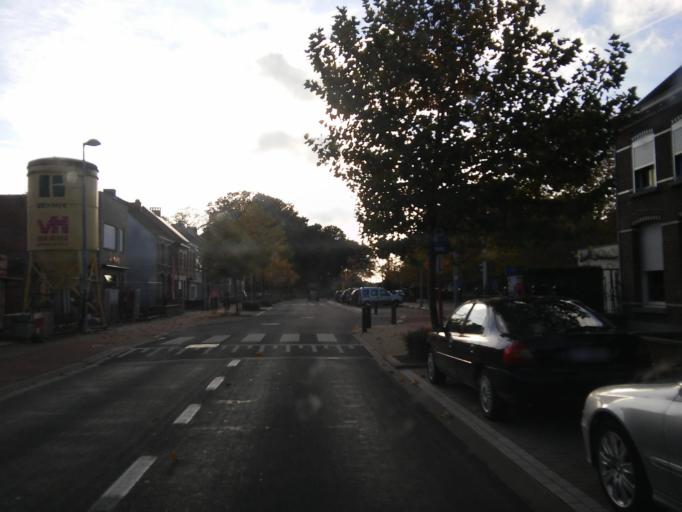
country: BE
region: Flanders
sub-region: Provincie Antwerpen
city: Berlaar
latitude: 51.1116
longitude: 4.6369
